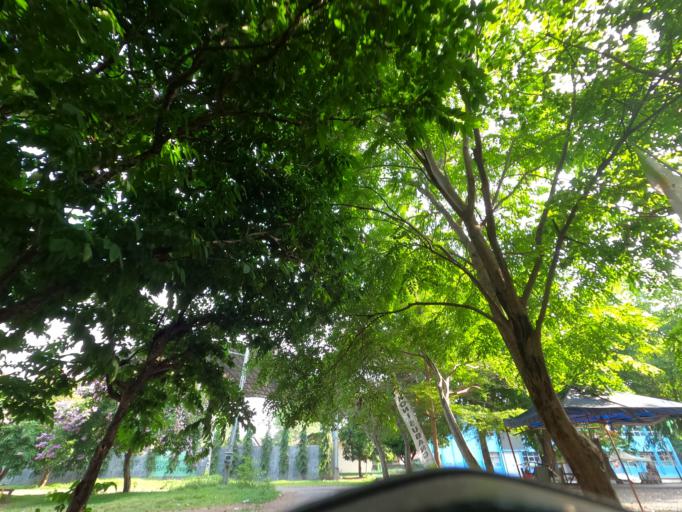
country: ID
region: West Java
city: Lembang
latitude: -6.5760
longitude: 107.7644
